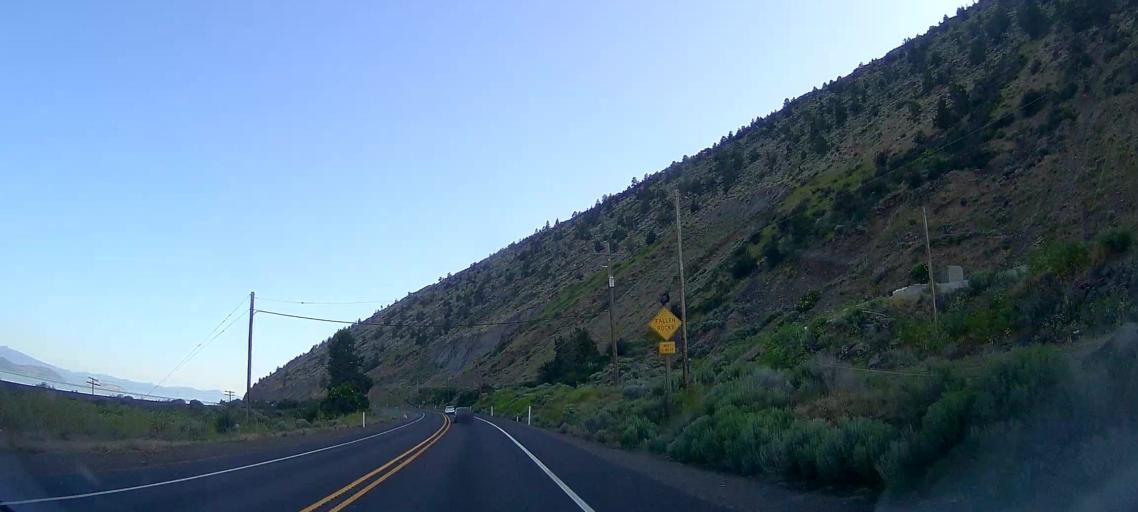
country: US
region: Oregon
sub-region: Klamath County
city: Klamath Falls
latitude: 42.3294
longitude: -121.8172
